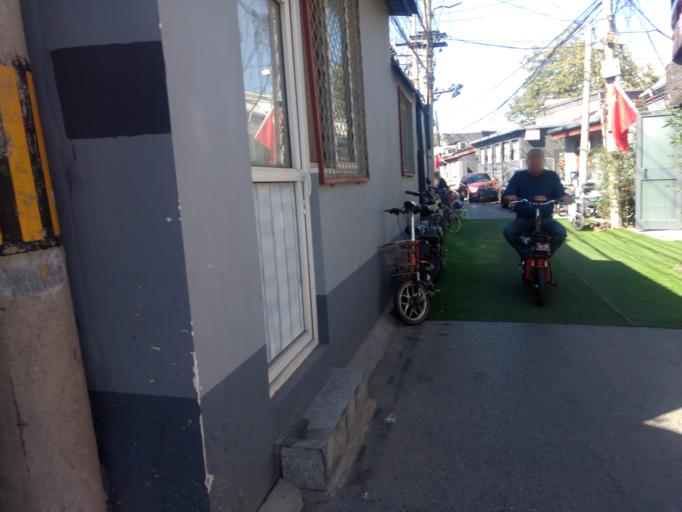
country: CN
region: Beijing
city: Beijing
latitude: 39.8917
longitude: 116.3835
